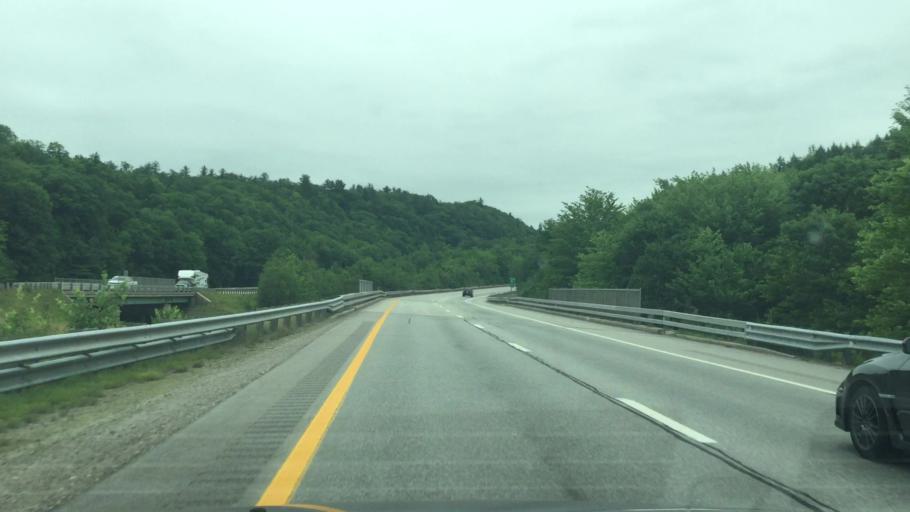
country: US
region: New Hampshire
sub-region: Merrimack County
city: Hill
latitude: 43.5780
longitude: -71.6252
